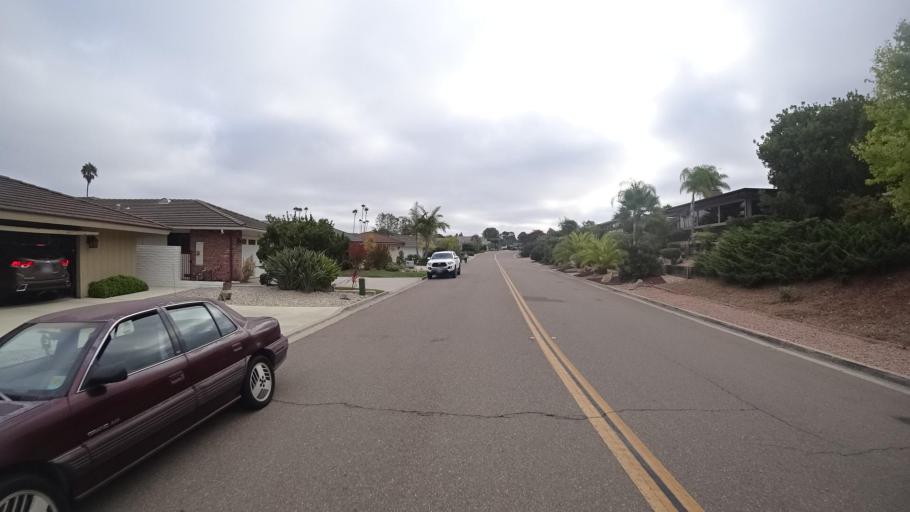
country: US
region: California
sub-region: San Diego County
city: Lake San Marcos
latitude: 33.1189
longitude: -117.2068
